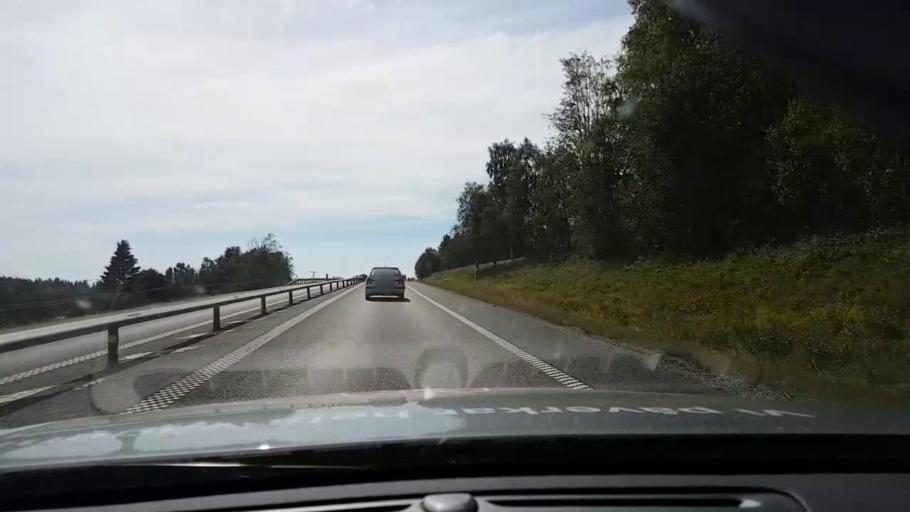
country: SE
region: Vaesternorrland
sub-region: OErnskoeldsviks Kommun
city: Ornskoldsvik
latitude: 63.3042
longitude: 18.9097
